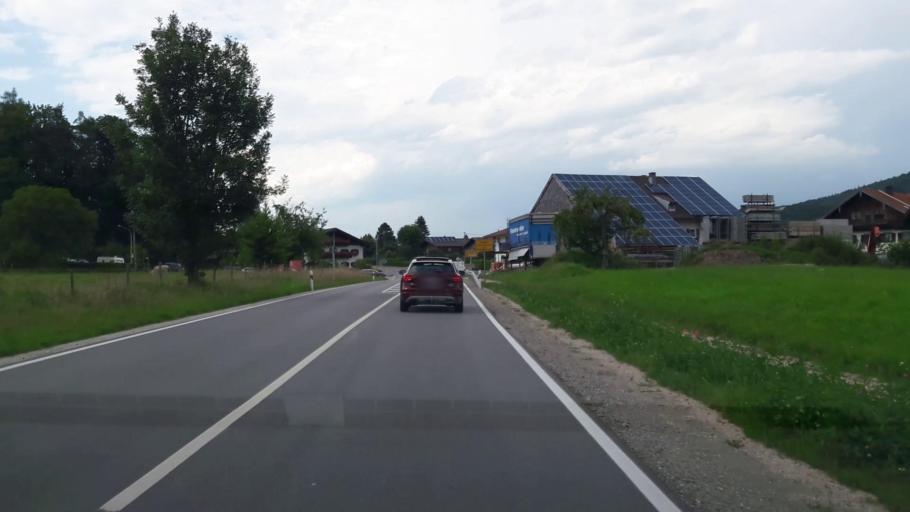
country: DE
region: Bavaria
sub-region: Upper Bavaria
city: Anger
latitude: 47.7989
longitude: 12.8662
